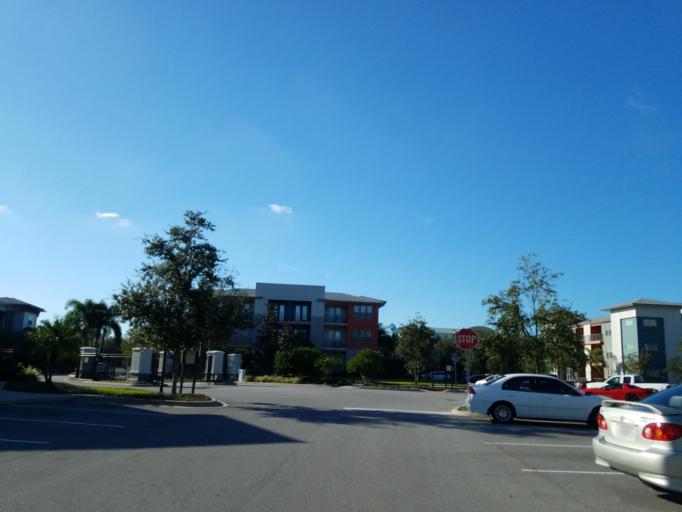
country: US
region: Florida
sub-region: Hillsborough County
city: Palm River-Clair Mel
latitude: 27.9386
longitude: -82.3362
